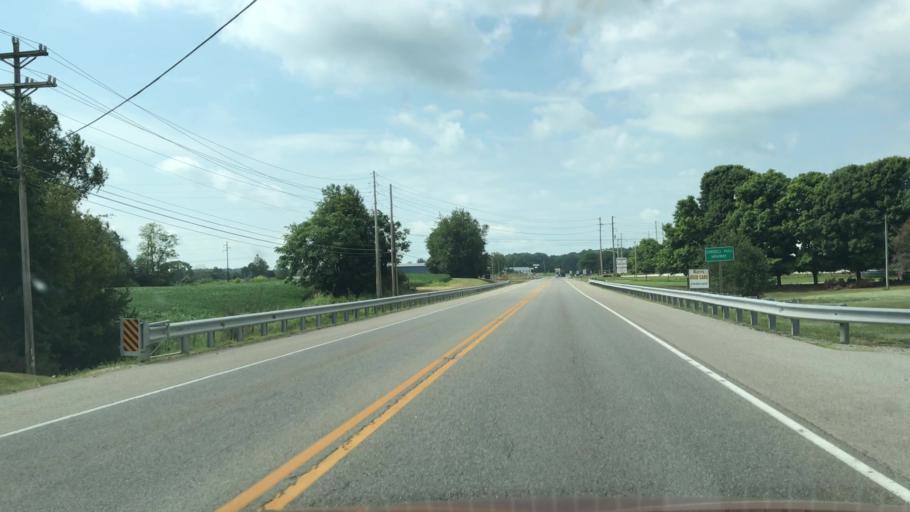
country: US
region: Kentucky
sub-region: Barren County
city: Cave City
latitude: 37.1230
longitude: -85.9618
